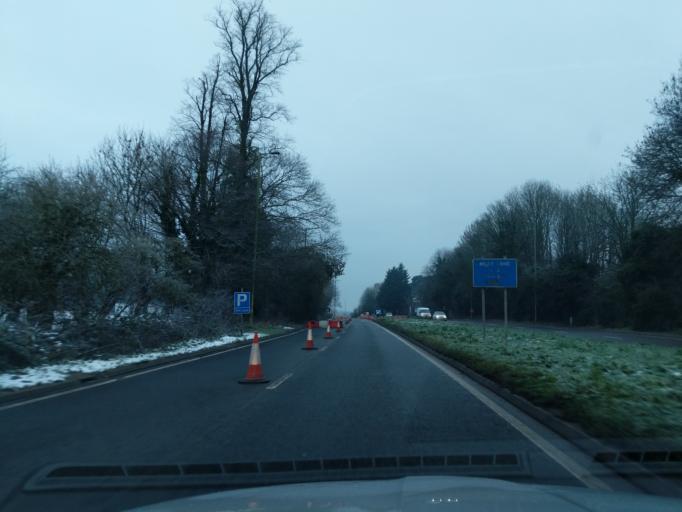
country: GB
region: England
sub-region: Hertfordshire
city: Abbots Langley
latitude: 51.6914
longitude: -0.4360
